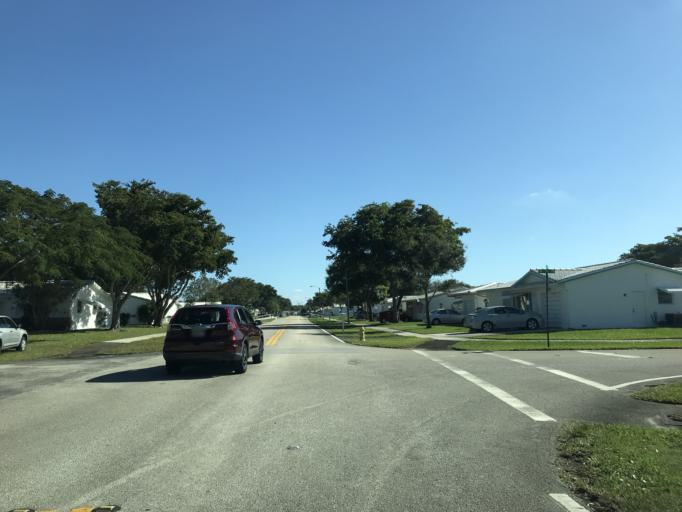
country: US
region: Florida
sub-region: Broward County
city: Plantation
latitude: 26.1441
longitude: -80.2687
